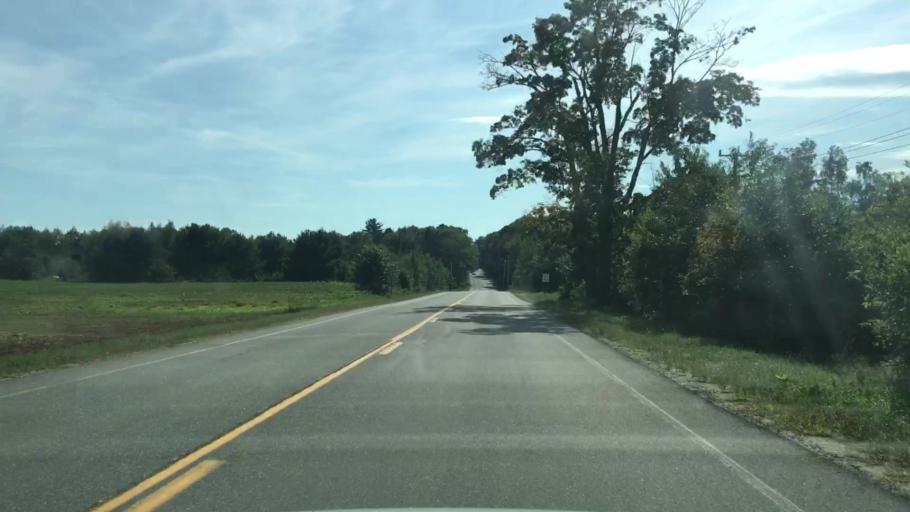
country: US
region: Maine
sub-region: Penobscot County
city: Lincoln
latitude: 45.4058
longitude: -68.5032
